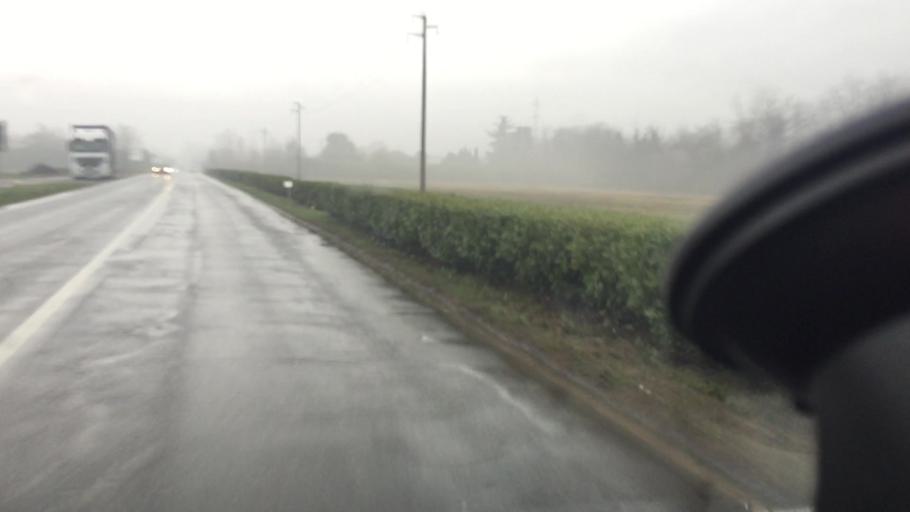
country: IT
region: Lombardy
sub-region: Citta metropolitana di Milano
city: Trezzo sull'Adda
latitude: 45.5939
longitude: 9.5224
